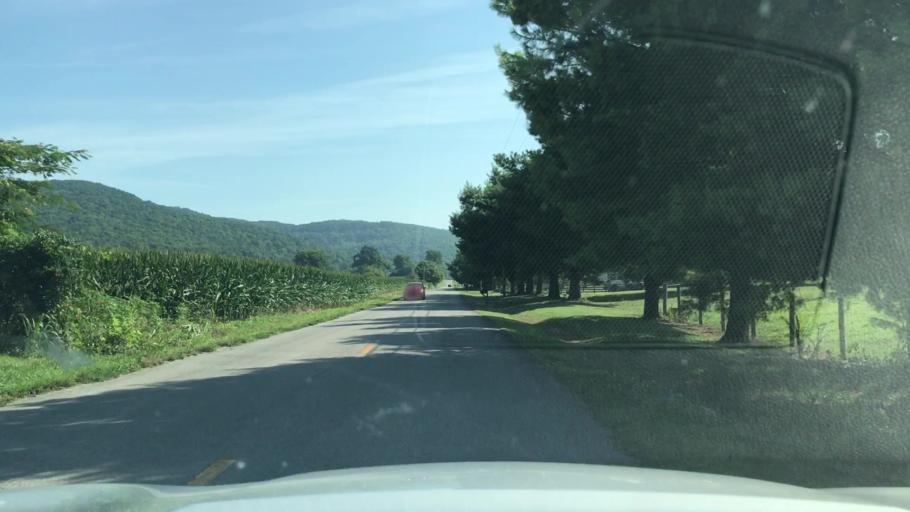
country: US
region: Kentucky
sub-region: Clinton County
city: Albany
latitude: 36.6961
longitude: -85.0444
